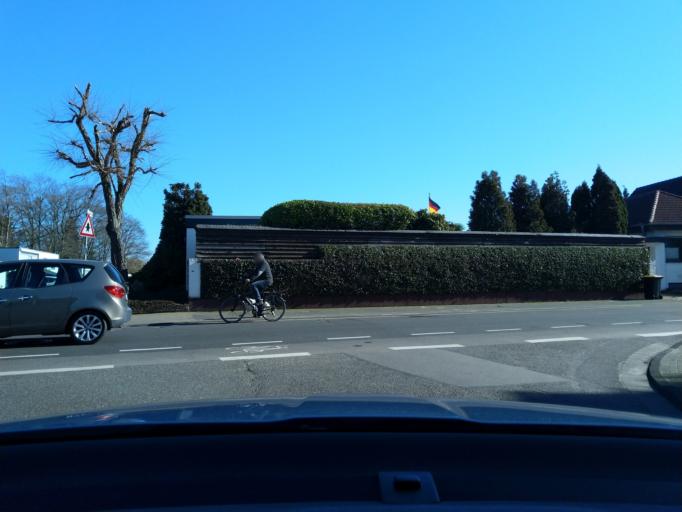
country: DE
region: North Rhine-Westphalia
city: Wegberg
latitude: 51.1488
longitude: 6.2806
